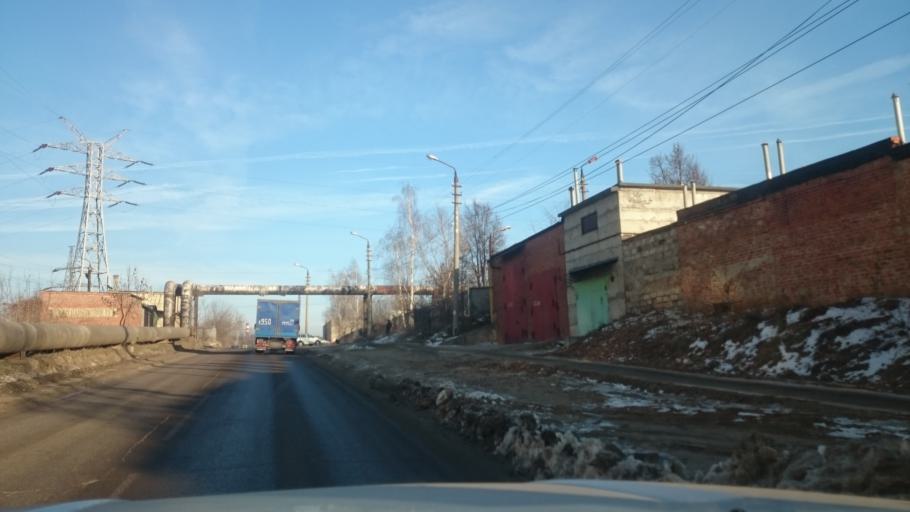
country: RU
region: Tula
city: Tula
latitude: 54.2144
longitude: 37.6856
